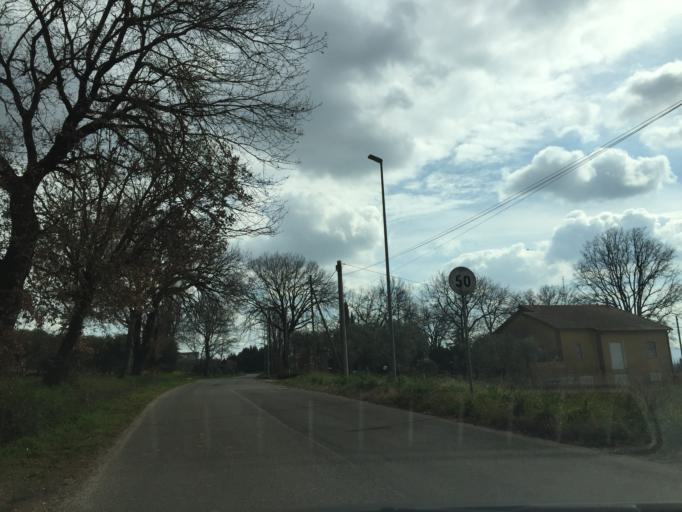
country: IT
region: Latium
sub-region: Provincia di Frosinone
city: Piedimonte San Germano Alta
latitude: 41.5031
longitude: 13.7349
